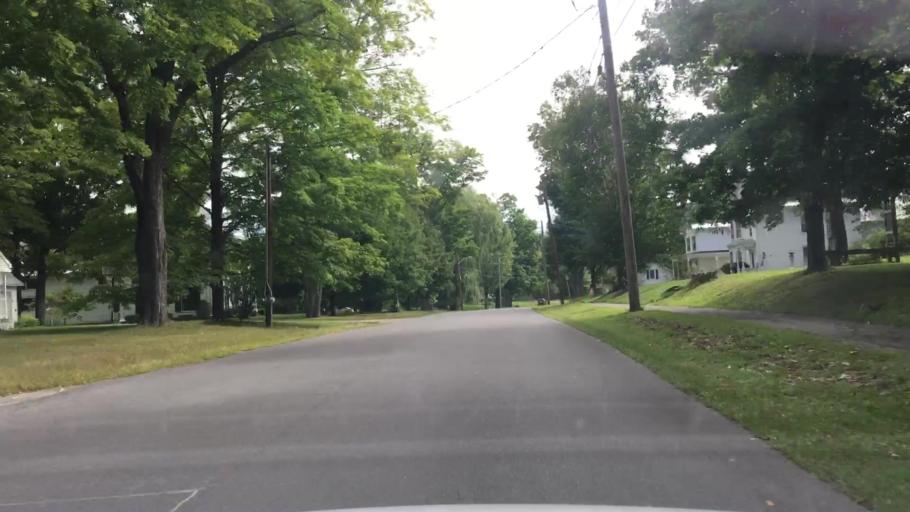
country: US
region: Maine
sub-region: Piscataquis County
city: Dover-Foxcroft
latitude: 45.1857
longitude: -69.2232
